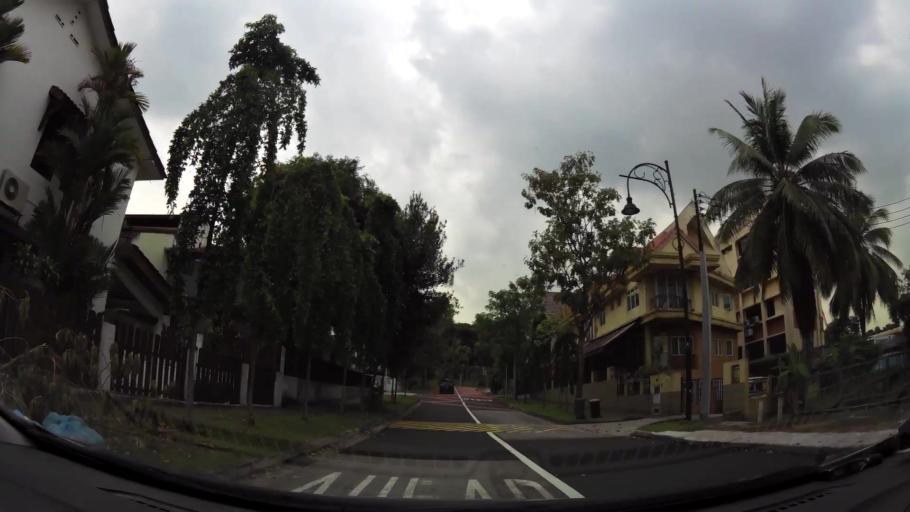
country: SG
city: Singapore
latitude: 1.3452
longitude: 103.8654
